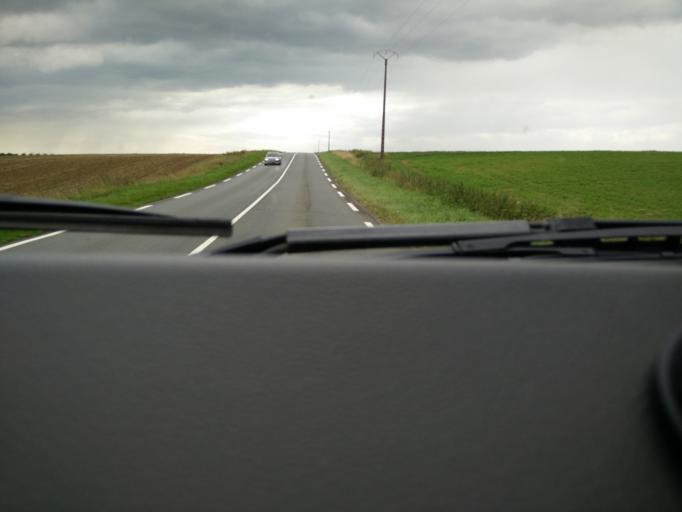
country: FR
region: Champagne-Ardenne
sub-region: Departement des Ardennes
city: Signy-le-Petit
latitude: 49.8674
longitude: 4.2055
